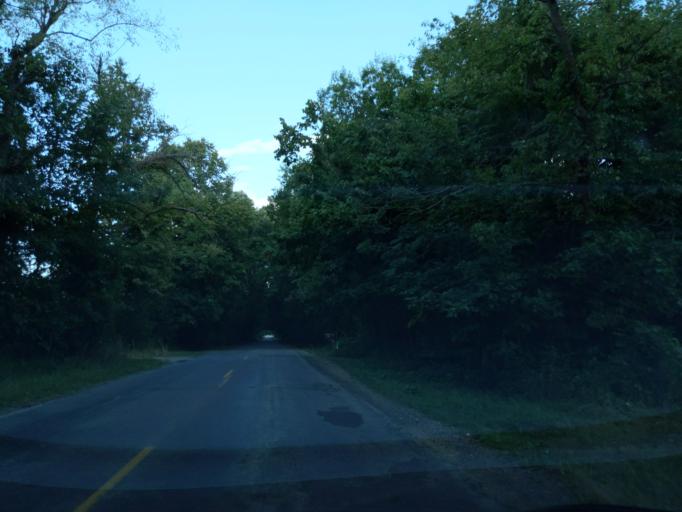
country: US
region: Michigan
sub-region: Ingham County
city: Holt
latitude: 42.6112
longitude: -84.5169
